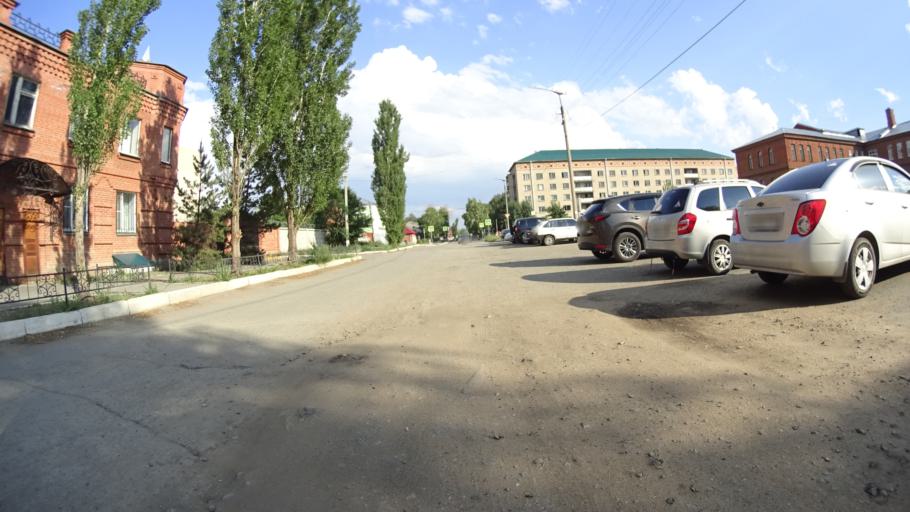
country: RU
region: Chelyabinsk
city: Troitsk
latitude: 54.0853
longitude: 61.5452
